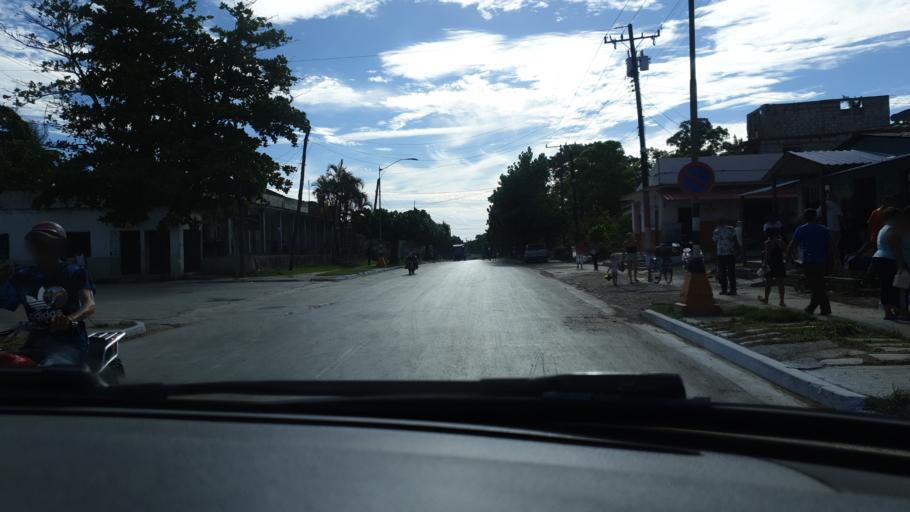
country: CU
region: Villa Clara
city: Santa Clara
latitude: 22.4131
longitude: -79.9529
